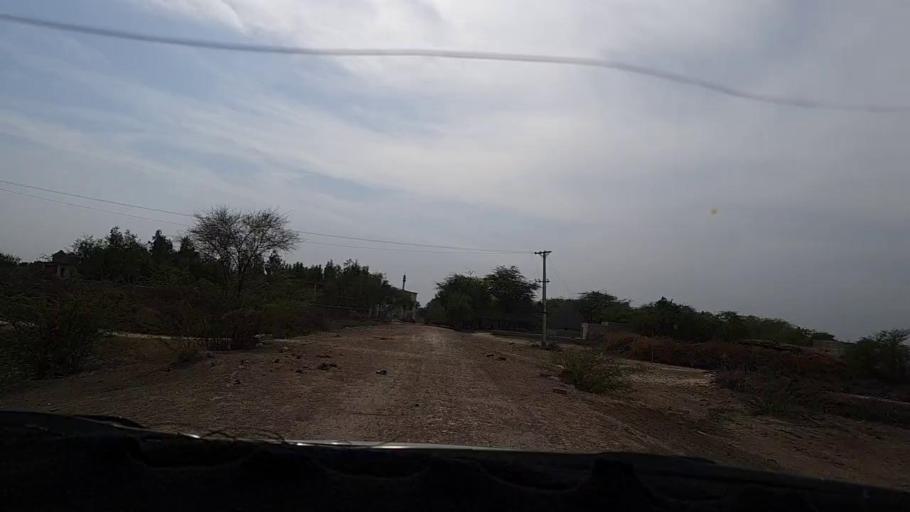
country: PK
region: Sindh
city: Pithoro
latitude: 25.5250
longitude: 69.3473
